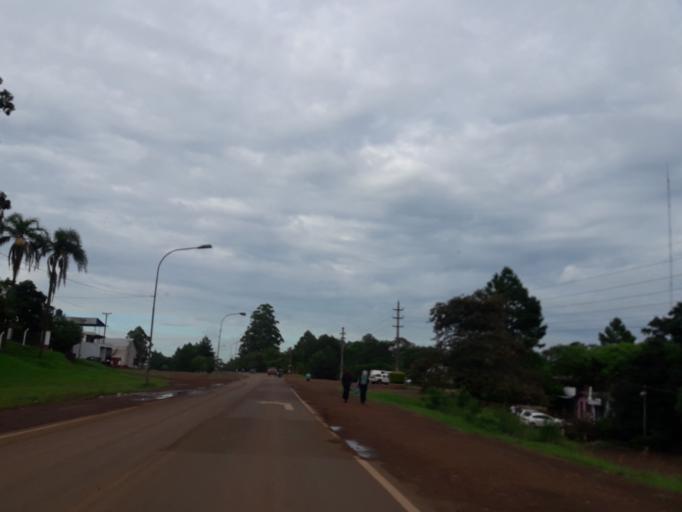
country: AR
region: Misiones
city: Bernardo de Irigoyen
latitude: -26.2626
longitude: -53.6519
